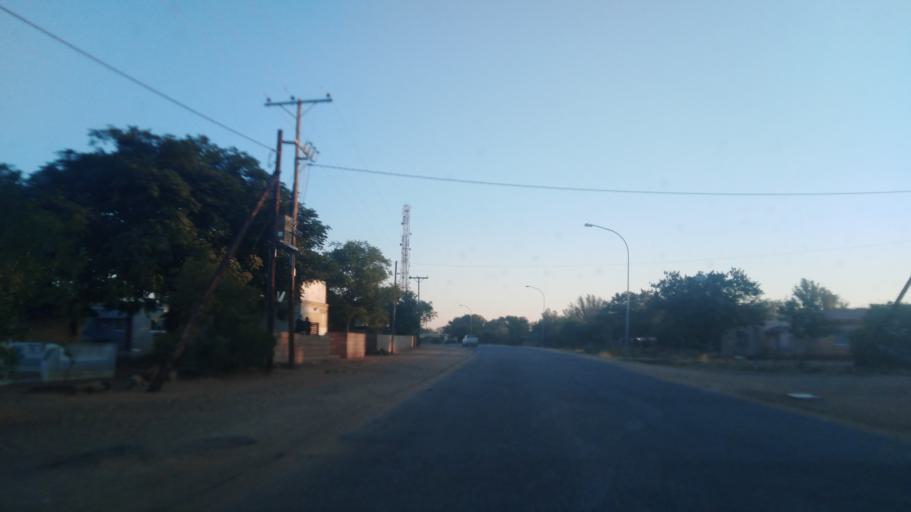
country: BW
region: Central
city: Mahalapye
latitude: -23.1136
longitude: 26.8304
